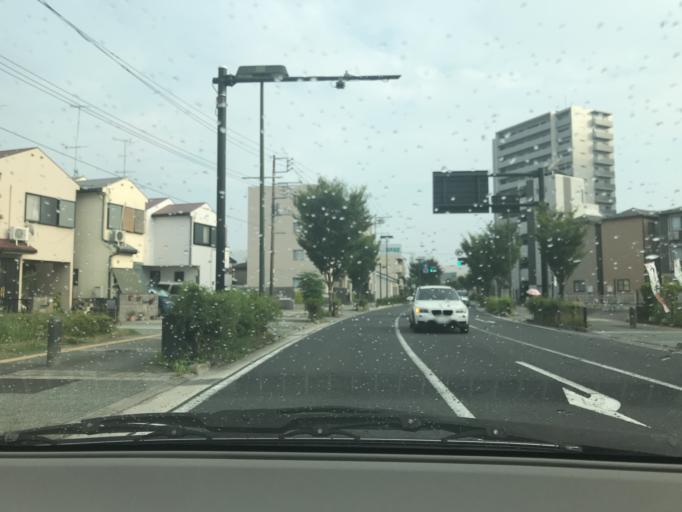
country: JP
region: Kanagawa
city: Fujisawa
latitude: 35.3443
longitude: 139.4461
